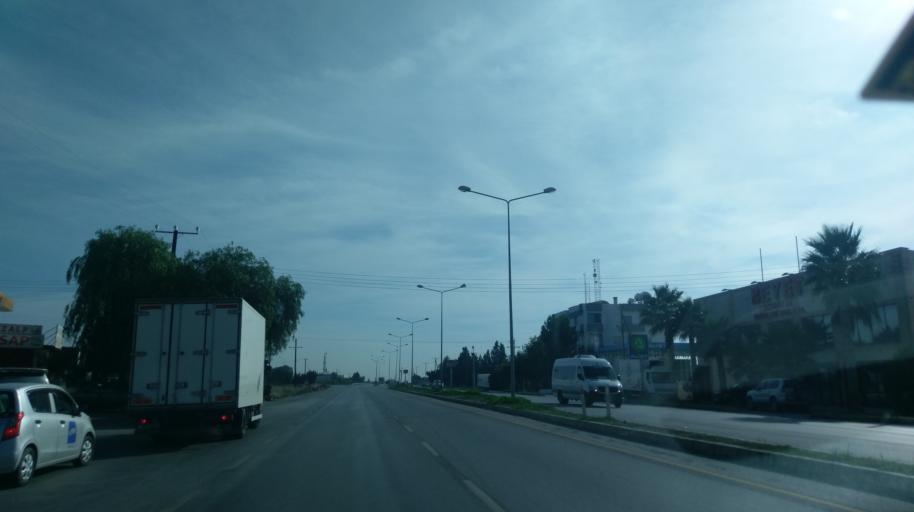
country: CY
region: Lefkosia
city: Geri
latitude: 35.2141
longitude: 33.5168
